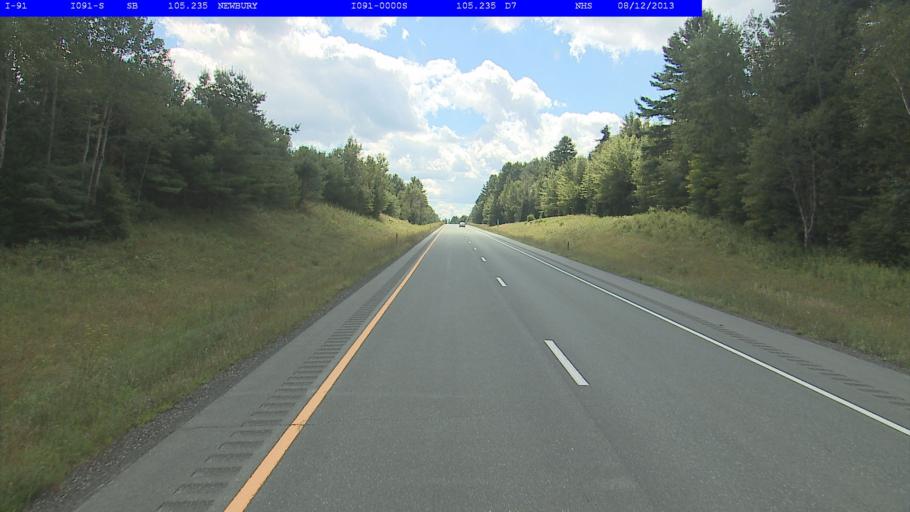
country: US
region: New Hampshire
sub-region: Grafton County
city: Haverhill
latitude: 44.0893
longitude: -72.1125
